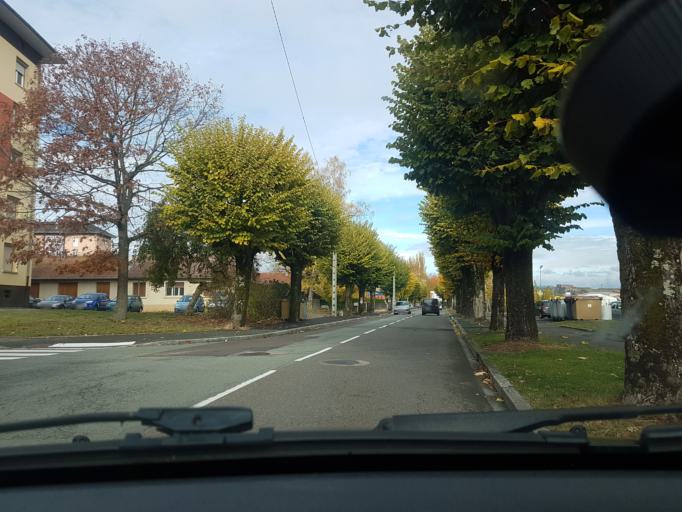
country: FR
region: Franche-Comte
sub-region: Territoire de Belfort
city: Danjoutin
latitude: 47.6206
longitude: 6.8513
